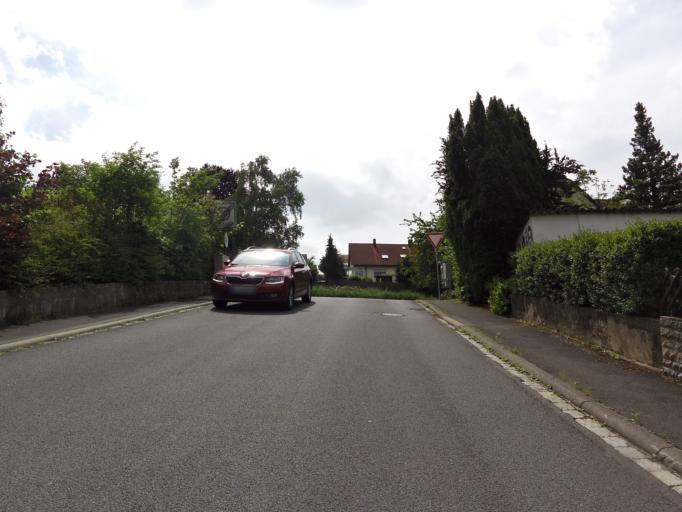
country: DE
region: Bavaria
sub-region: Regierungsbezirk Unterfranken
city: Waldbrunn
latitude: 49.7593
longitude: 9.8071
